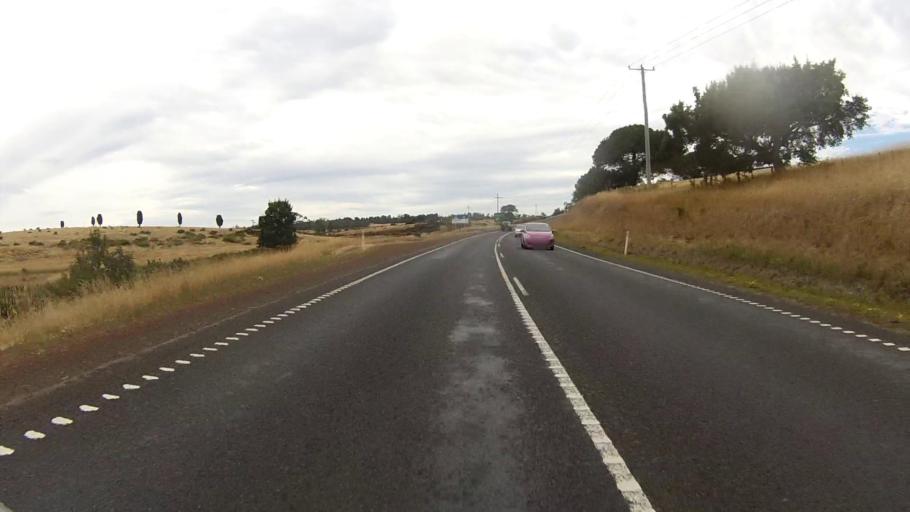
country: AU
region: Tasmania
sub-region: Northern Midlands
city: Evandale
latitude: -41.8449
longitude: 147.4485
